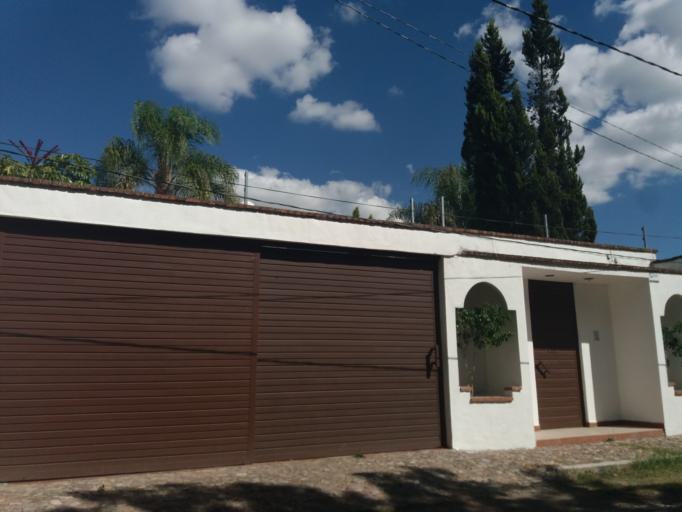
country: MX
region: Aguascalientes
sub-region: Aguascalientes
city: San Sebastian [Fraccionamiento]
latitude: 21.7889
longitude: -102.2795
